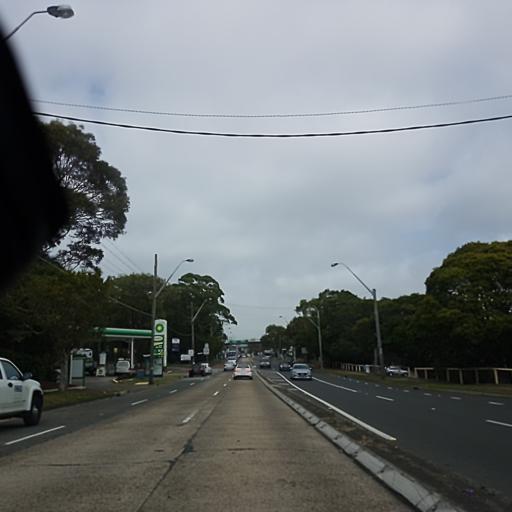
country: AU
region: New South Wales
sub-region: Manly Vale
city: Balgowlah
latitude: -33.7950
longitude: 151.2565
